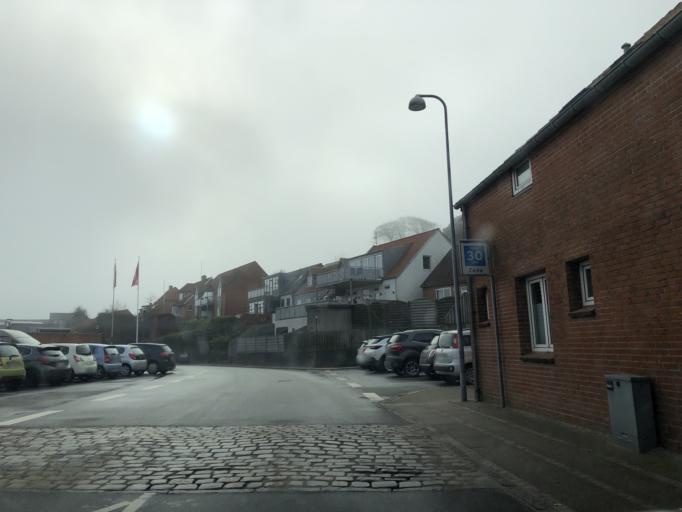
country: DK
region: Central Jutland
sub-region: Lemvig Kommune
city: Lemvig
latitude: 56.5493
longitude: 8.3058
